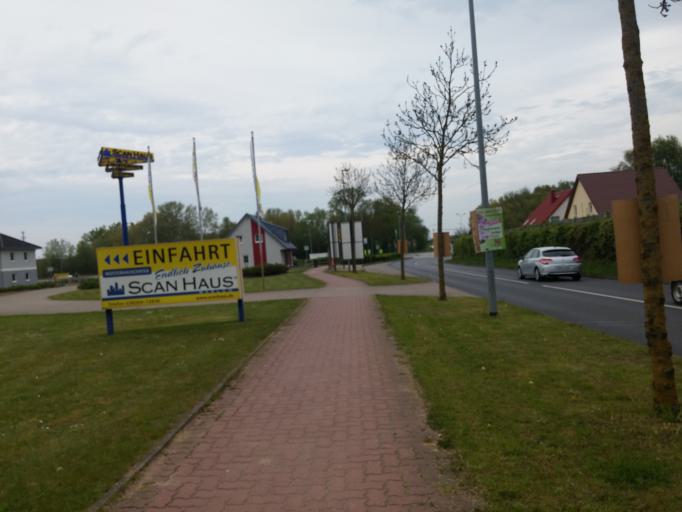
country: DE
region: Mecklenburg-Vorpommern
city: Roggentin
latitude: 54.0794
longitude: 12.1981
